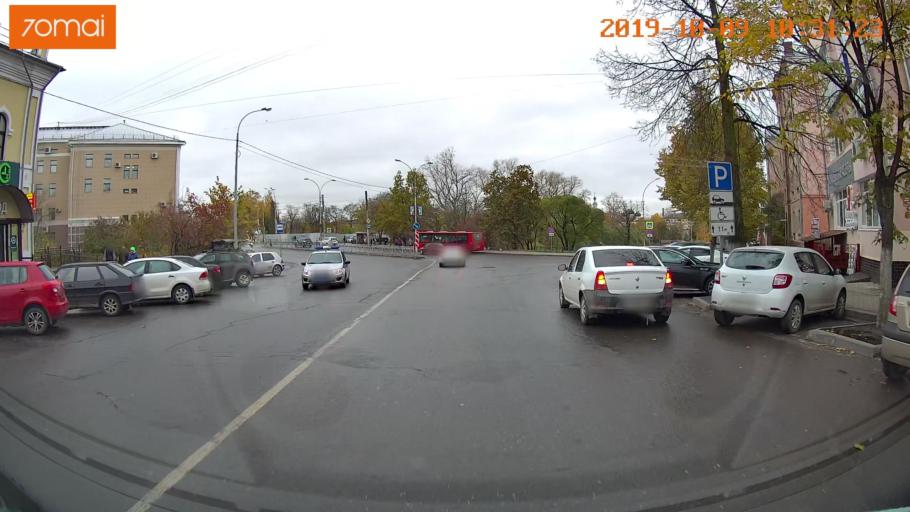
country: RU
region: Vologda
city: Vologda
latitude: 59.2217
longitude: 39.8932
